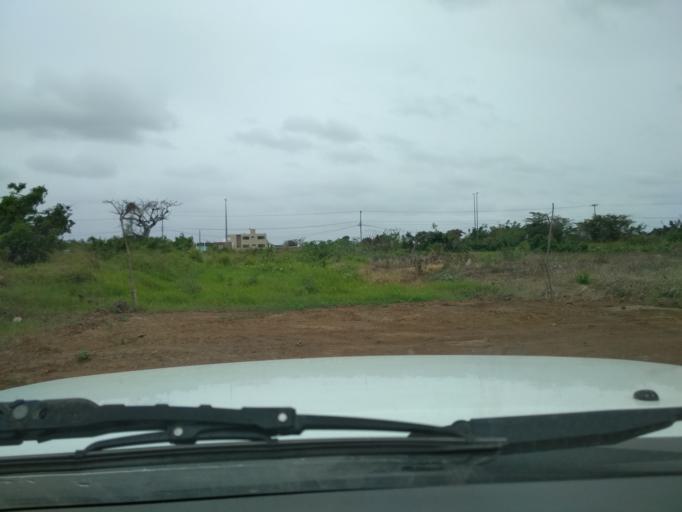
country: MX
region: Veracruz
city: Paso del Toro
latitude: 19.0448
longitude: -96.1329
